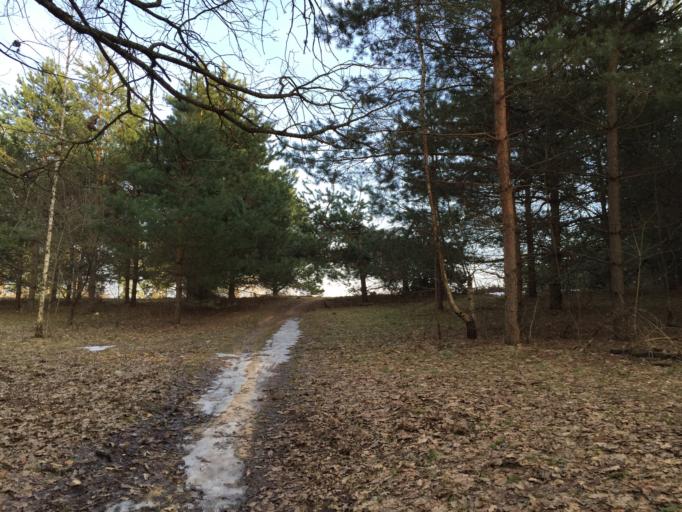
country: LV
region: Stopini
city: Ulbroka
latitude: 56.9635
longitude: 24.2890
